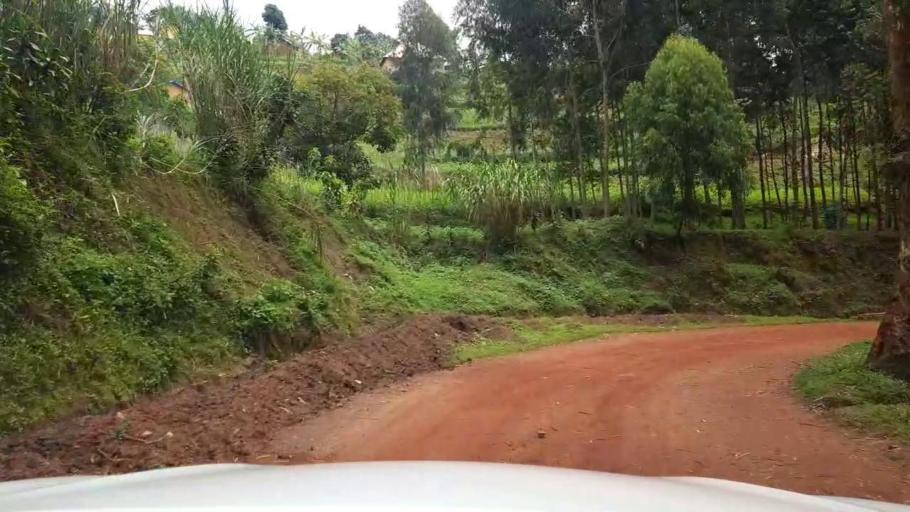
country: UG
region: Western Region
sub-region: Kisoro District
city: Kisoro
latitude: -1.4176
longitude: 29.8301
